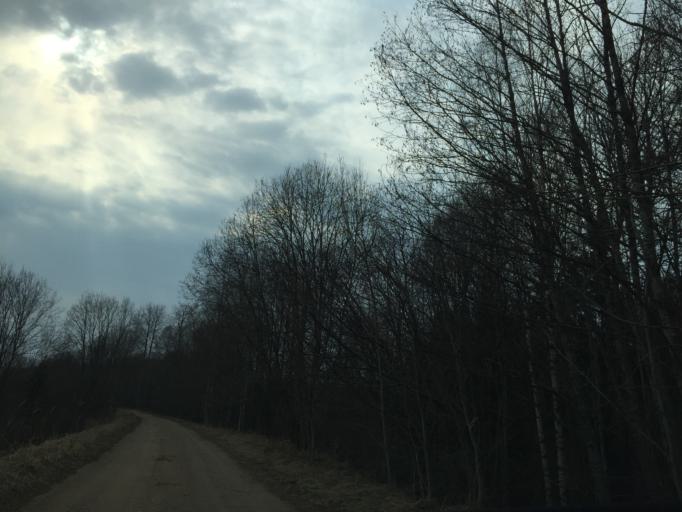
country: LV
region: Priekuli
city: Priekuli
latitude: 57.2059
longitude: 25.3934
